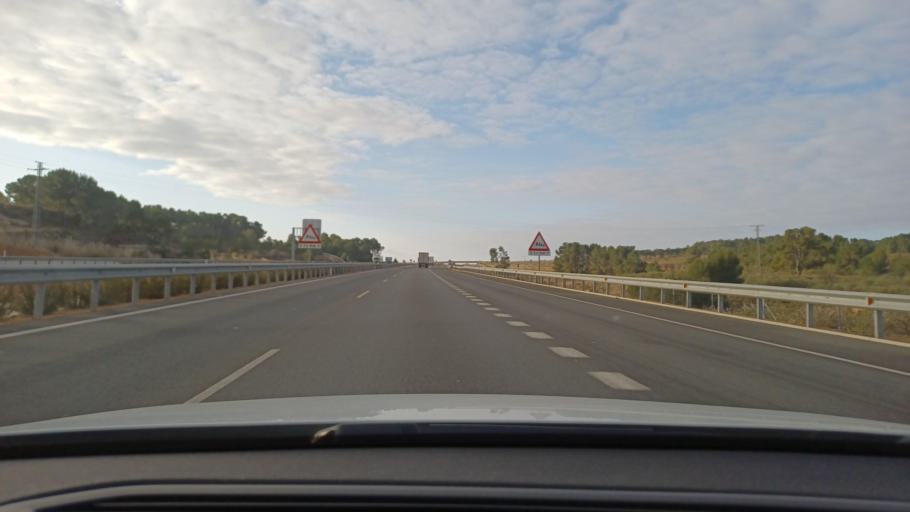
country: ES
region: Valencia
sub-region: Provincia de Valencia
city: La Font de la Figuera
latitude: 38.7781
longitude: -0.8931
